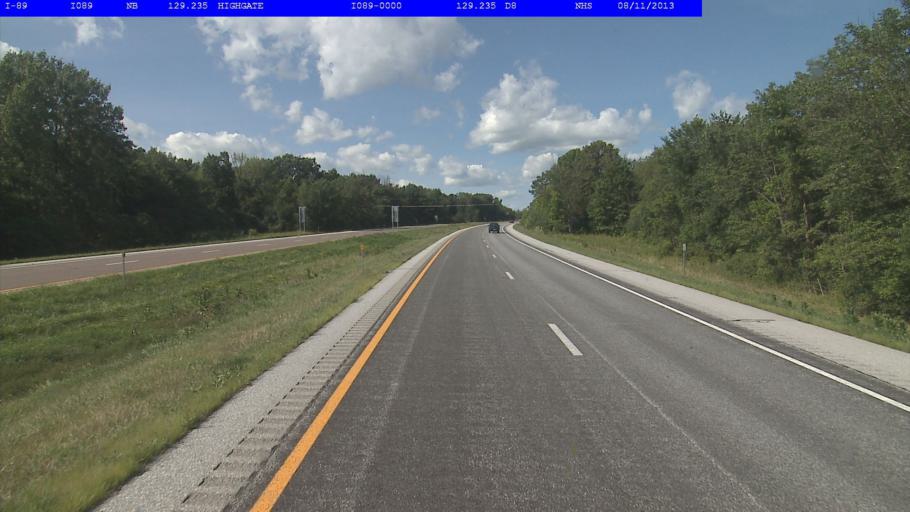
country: US
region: Vermont
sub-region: Franklin County
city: Swanton
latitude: 45.0009
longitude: -73.0867
